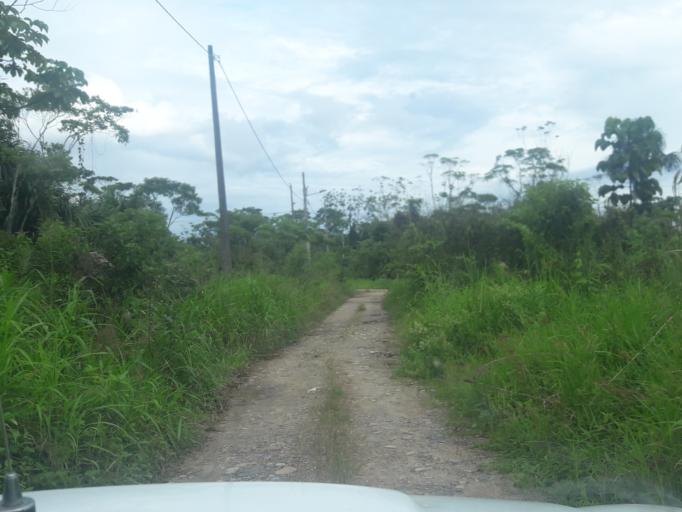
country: EC
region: Napo
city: Archidona
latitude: -0.9512
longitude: -77.8148
